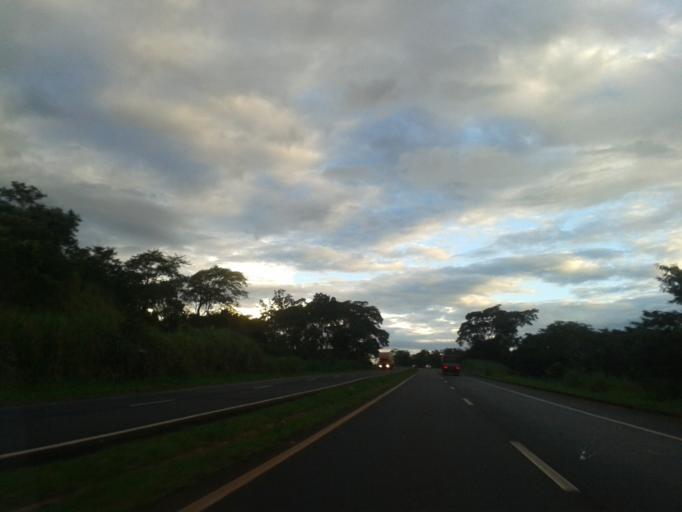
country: BR
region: Minas Gerais
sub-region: Centralina
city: Centralina
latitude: -18.6276
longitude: -49.1851
